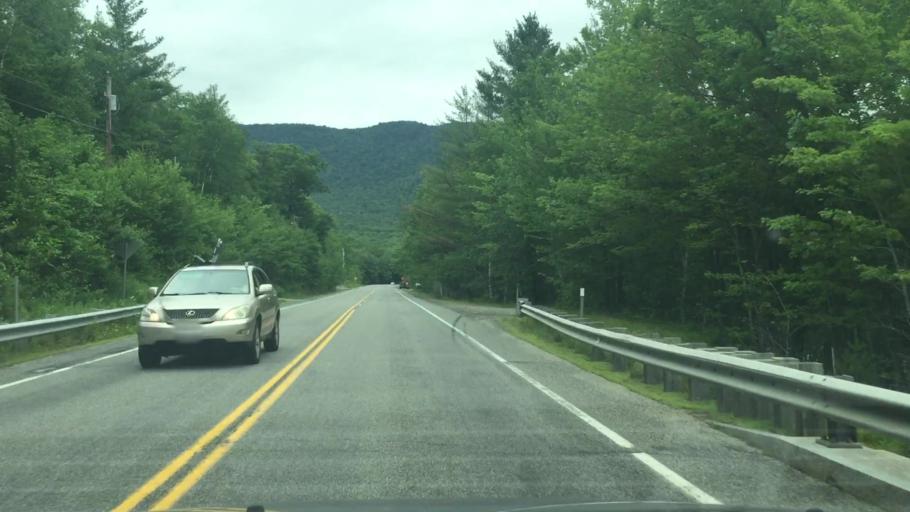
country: US
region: New Hampshire
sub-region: Carroll County
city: North Conway
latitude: 44.1364
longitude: -71.3609
